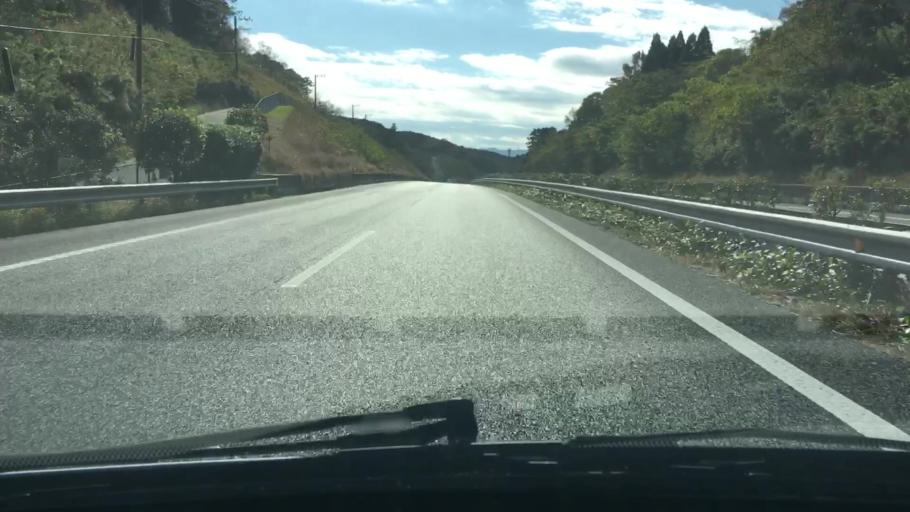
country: JP
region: Chiba
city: Kisarazu
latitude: 35.3331
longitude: 139.9454
